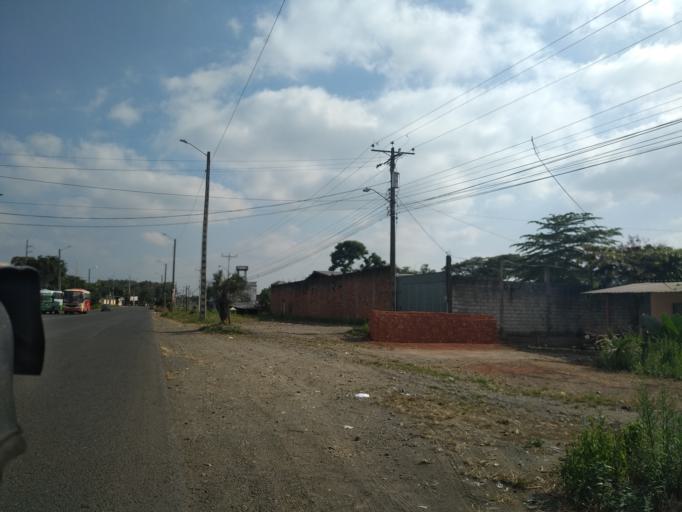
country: EC
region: Los Rios
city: Quevedo
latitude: -1.0643
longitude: -79.4920
